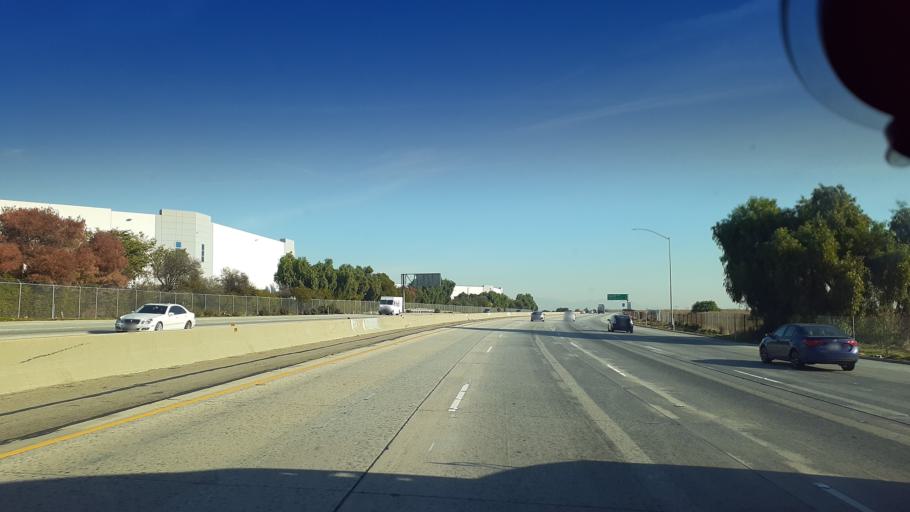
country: US
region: California
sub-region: Los Angeles County
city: San Pedro
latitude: 33.7599
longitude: -118.2885
